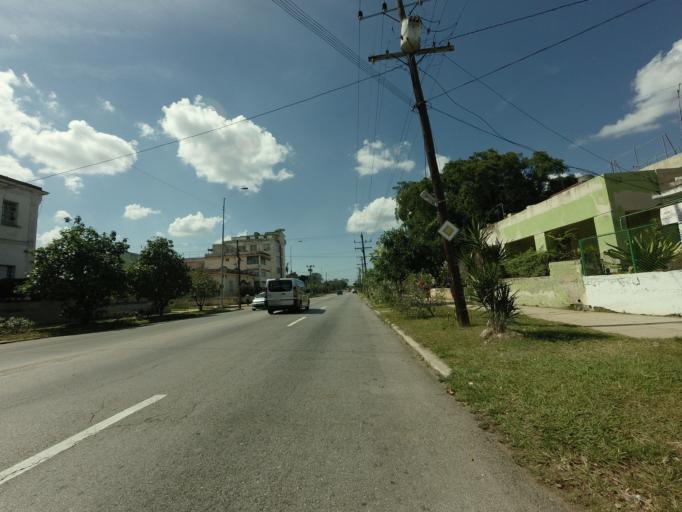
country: CU
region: La Habana
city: Havana
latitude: 23.1126
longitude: -82.4205
